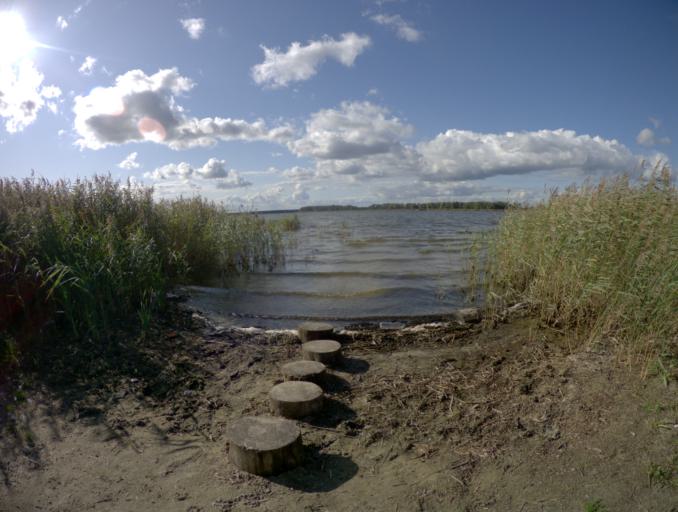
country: RU
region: Moskovskaya
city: Kerva
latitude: 55.6103
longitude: 39.5688
